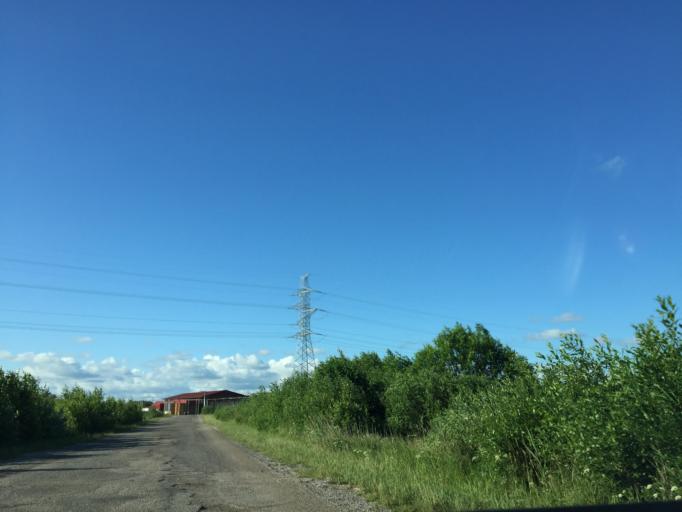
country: LV
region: Ventspils
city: Ventspils
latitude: 57.3994
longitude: 21.6492
